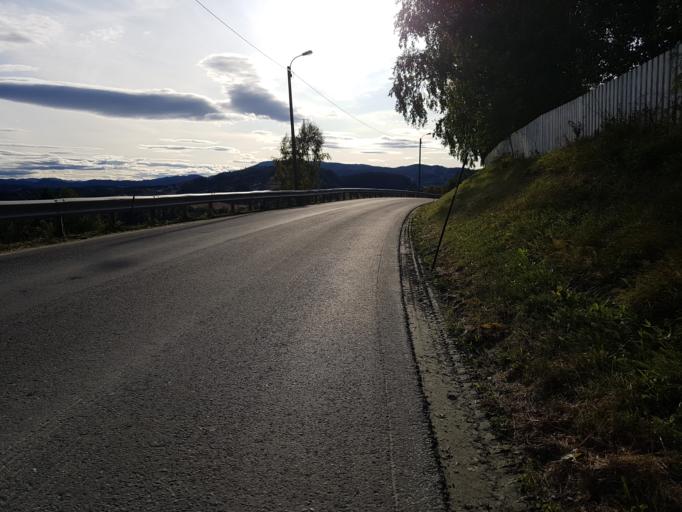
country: NO
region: Sor-Trondelag
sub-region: Klaebu
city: Klaebu
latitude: 63.3472
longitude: 10.4819
